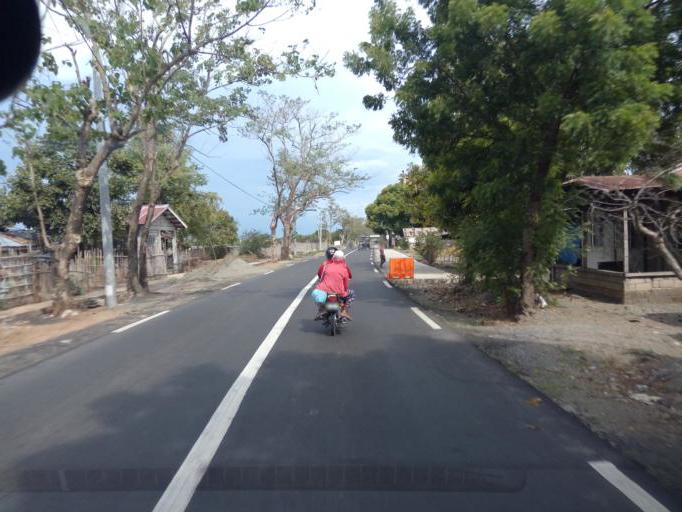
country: PH
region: Central Luzon
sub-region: Province of Nueva Ecija
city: Parista
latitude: 15.8261
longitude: 120.9503
